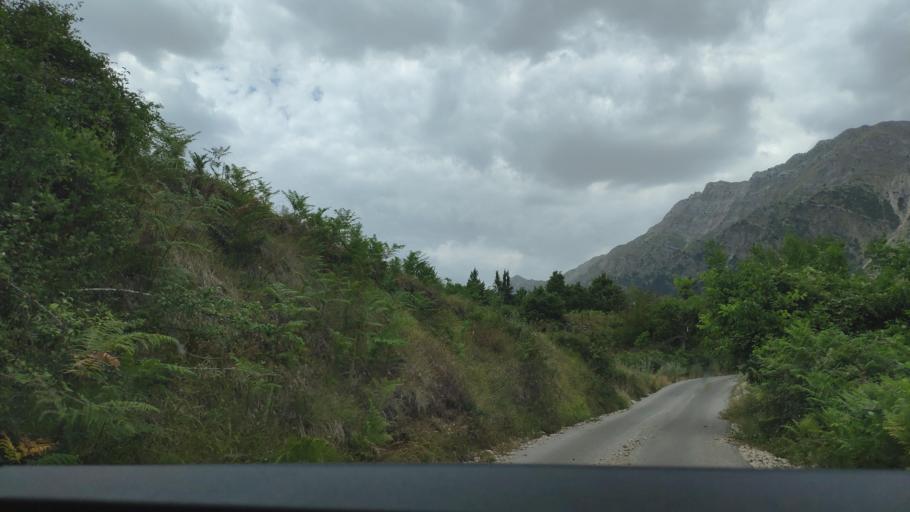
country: GR
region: Epirus
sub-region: Nomos Artas
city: Voulgareli
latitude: 39.4383
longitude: 21.2047
